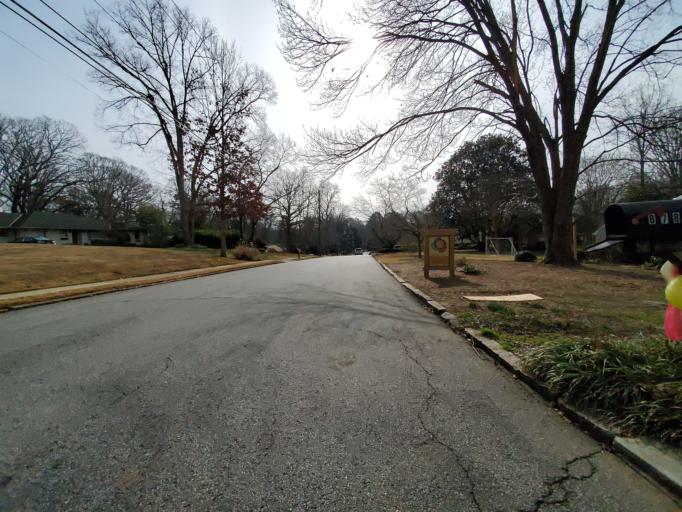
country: US
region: Georgia
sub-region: DeKalb County
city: North Decatur
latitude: 33.7760
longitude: -84.3164
